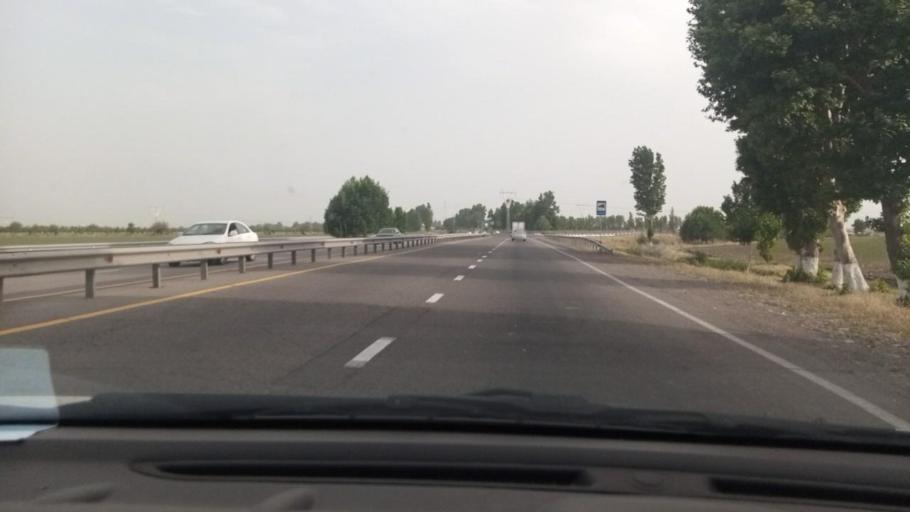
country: UZ
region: Toshkent Shahri
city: Bektemir
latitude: 41.1913
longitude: 69.4031
